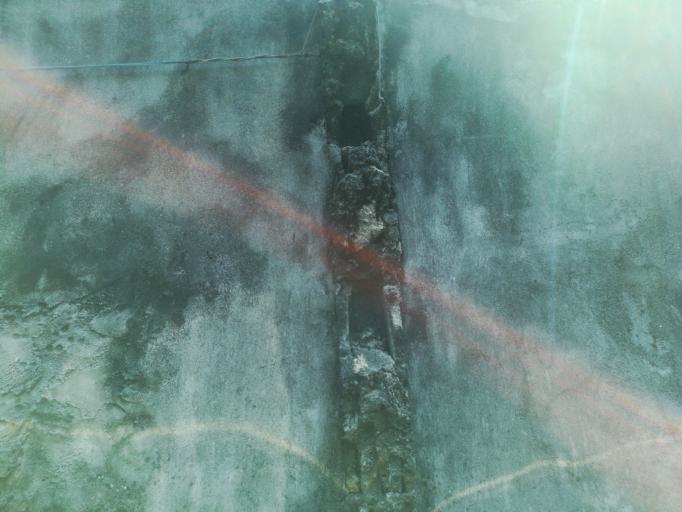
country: NG
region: Rivers
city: Port Harcourt
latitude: 4.8205
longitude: 6.9827
